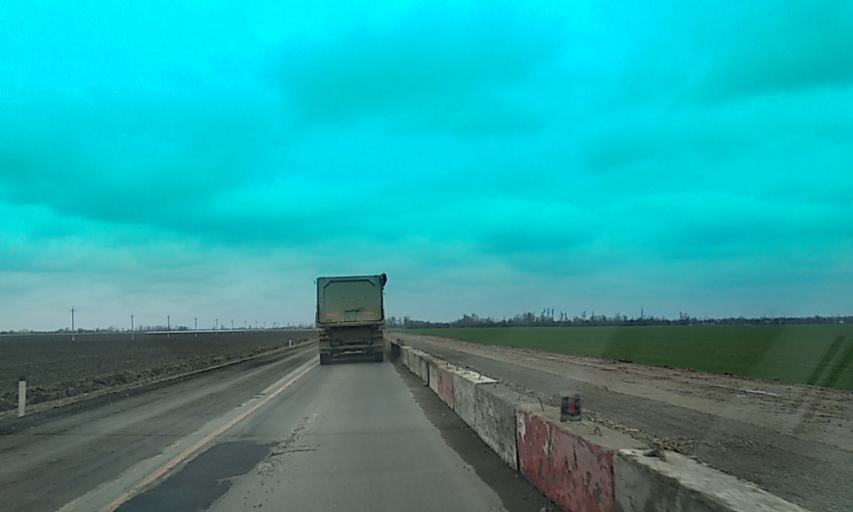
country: RU
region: Adygeya
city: Beloye
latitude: 45.0221
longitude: 39.6888
